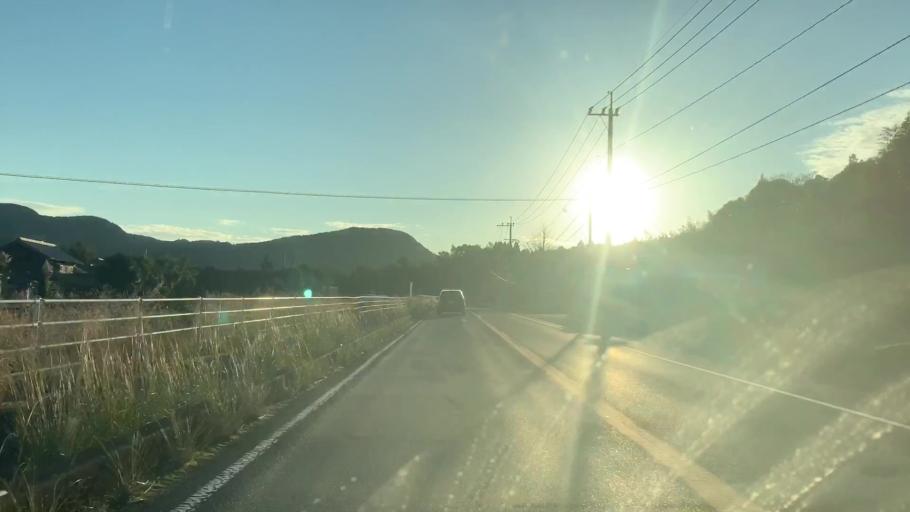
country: JP
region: Saga Prefecture
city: Karatsu
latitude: 33.3431
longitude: 129.9910
